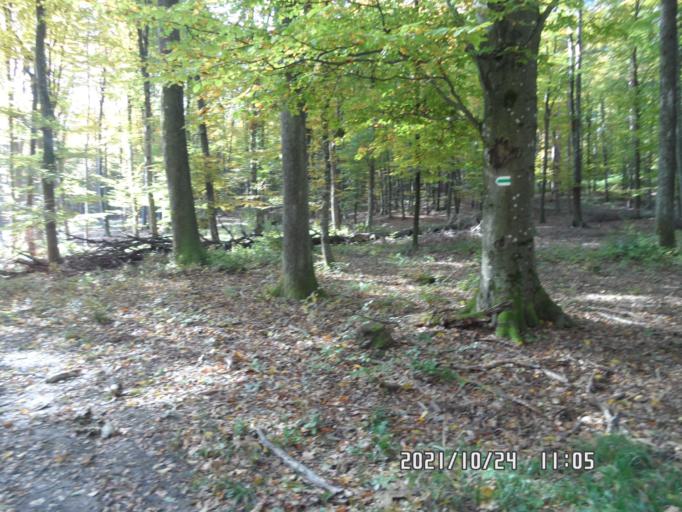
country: SI
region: Hodos-Hodos
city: Hodos
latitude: 46.8073
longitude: 16.3435
